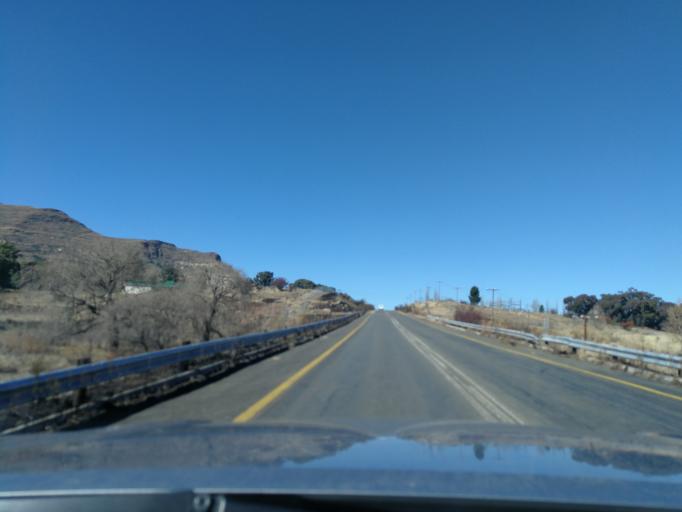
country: ZA
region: Orange Free State
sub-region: Thabo Mofutsanyana District Municipality
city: Bethlehem
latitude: -28.5137
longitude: 28.4313
